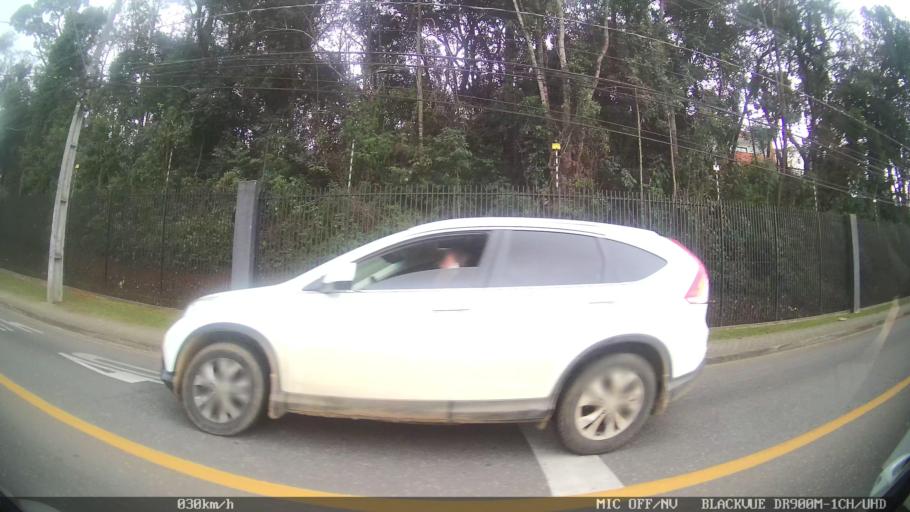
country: BR
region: Parana
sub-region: Curitiba
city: Curitiba
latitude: -25.3744
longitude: -49.2722
